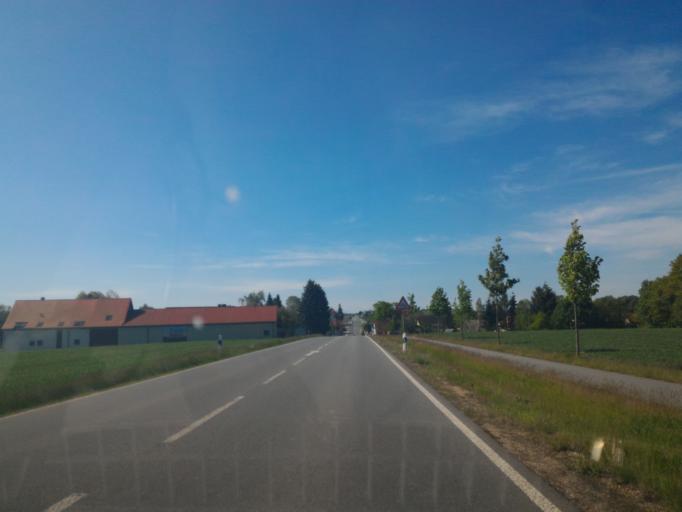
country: DE
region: Saxony
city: Neugersdorf
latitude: 51.0072
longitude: 14.6198
